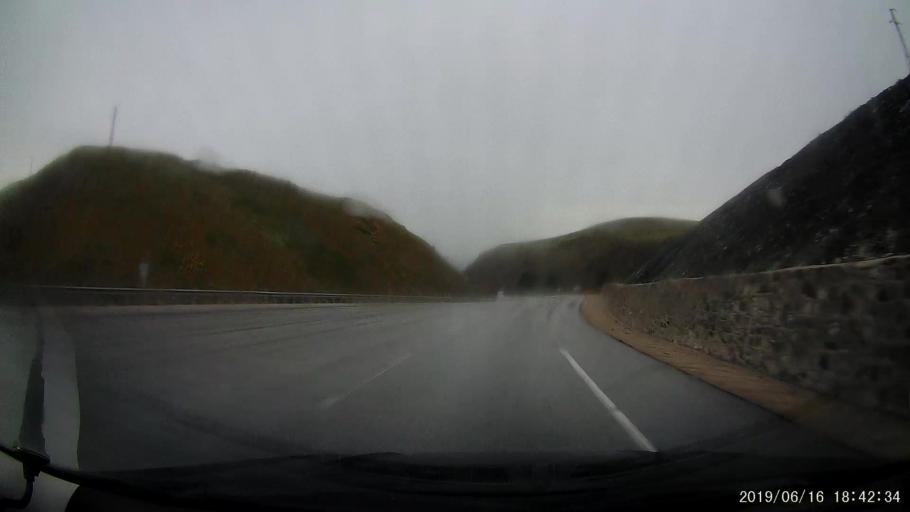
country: TR
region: Erzincan
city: Doganbeyli
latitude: 39.8679
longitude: 39.1068
